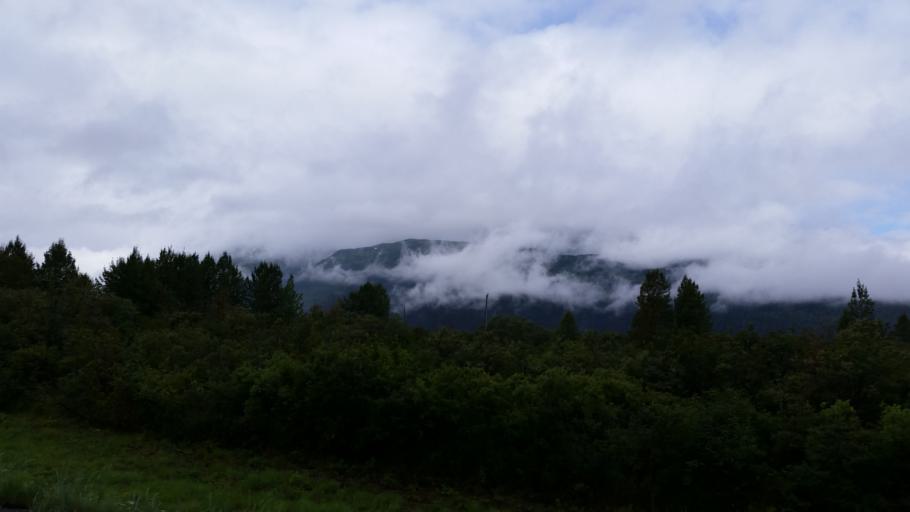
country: US
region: Alaska
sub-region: Anchorage Municipality
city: Girdwood
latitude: 60.8311
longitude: -148.9793
